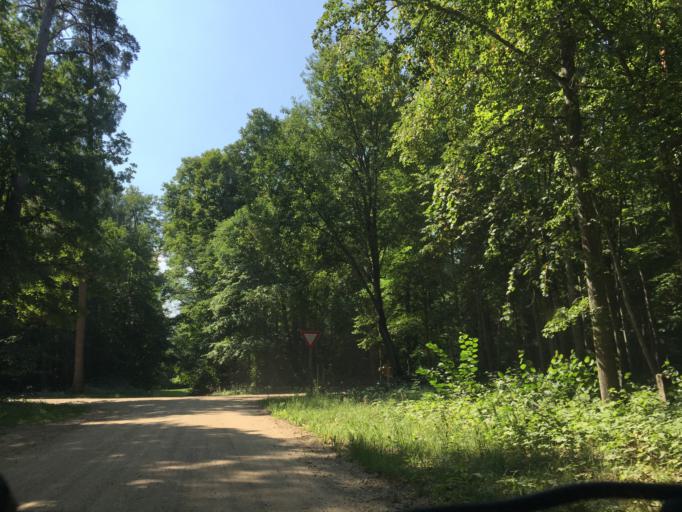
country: LV
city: Tervete
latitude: 56.4827
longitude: 23.3973
